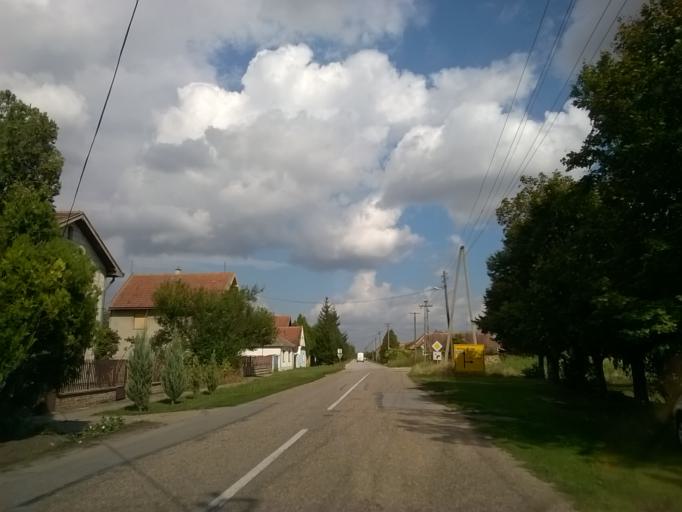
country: RS
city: Jermenovci
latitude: 45.1842
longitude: 21.0364
